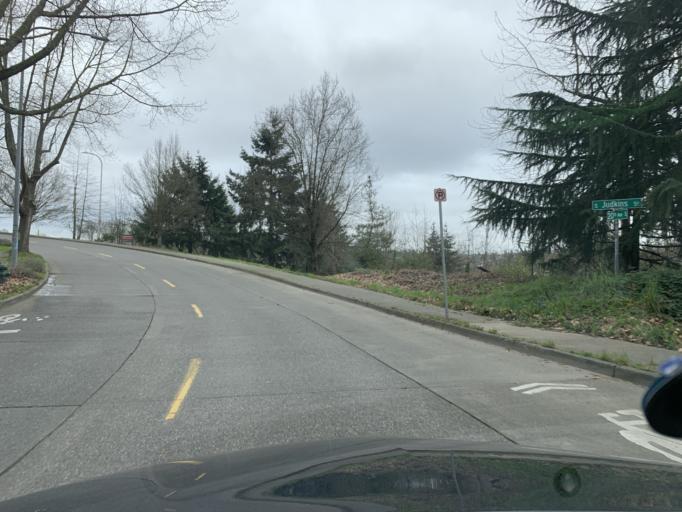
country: US
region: Washington
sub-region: King County
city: Seattle
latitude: 47.5925
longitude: -122.3062
